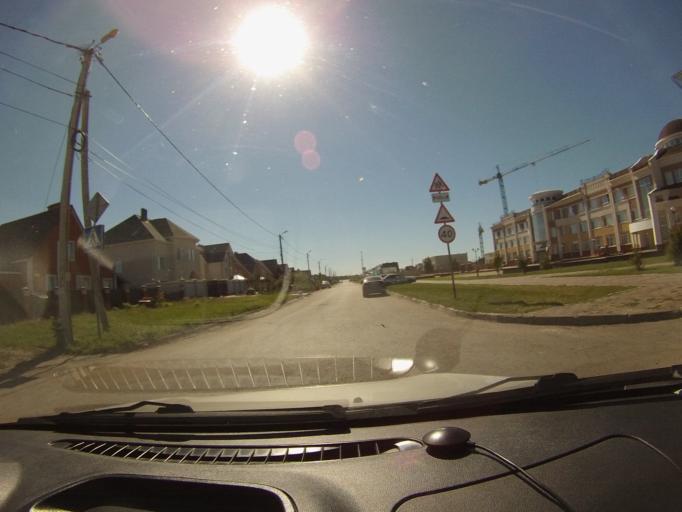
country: RU
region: Tambov
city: Tambov
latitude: 52.7696
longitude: 41.3846
